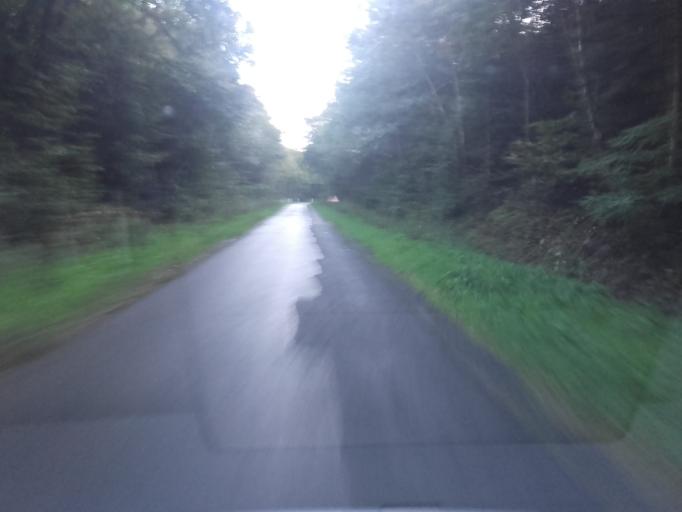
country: FR
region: Brittany
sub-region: Departement des Cotes-d'Armor
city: Pleguien
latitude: 48.6539
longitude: -2.9345
